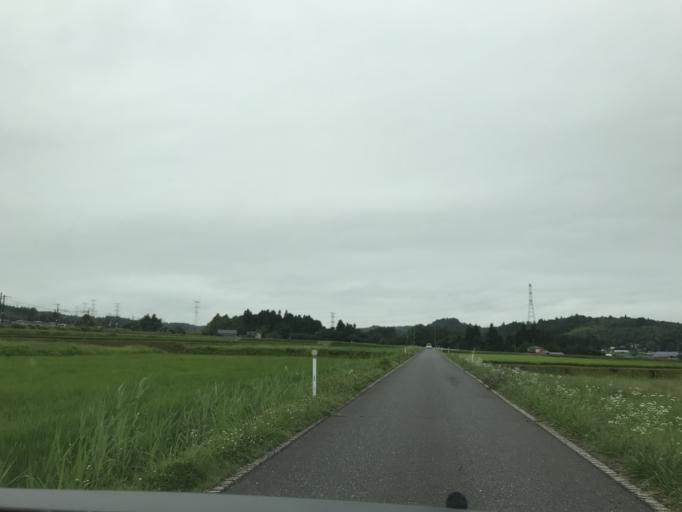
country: JP
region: Iwate
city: Ichinoseki
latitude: 38.8560
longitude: 141.1547
